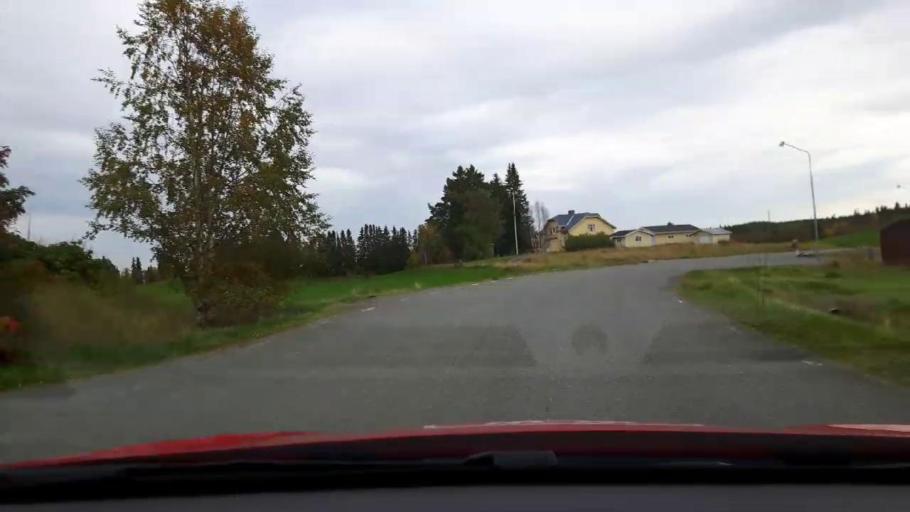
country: SE
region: Jaemtland
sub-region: Krokoms Kommun
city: Krokom
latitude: 63.2260
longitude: 14.1336
